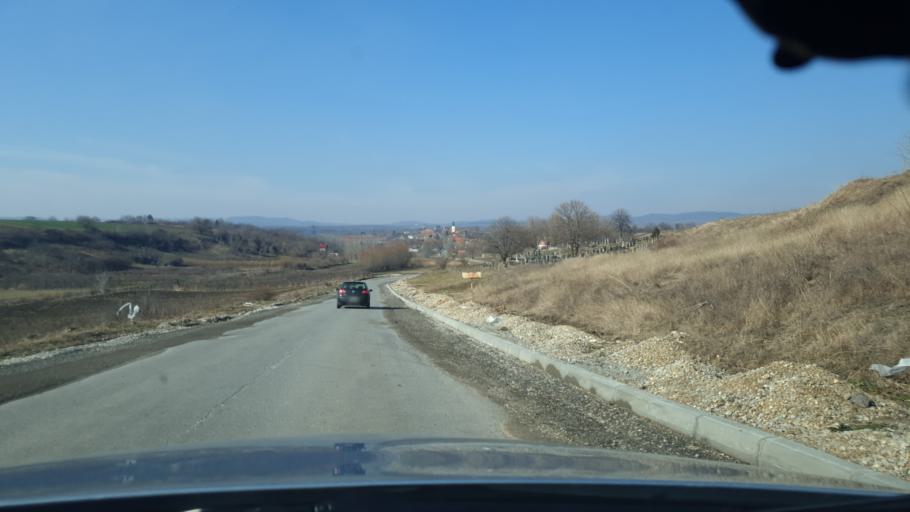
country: RS
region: Autonomna Pokrajina Vojvodina
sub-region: Sremski Okrug
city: Irig
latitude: 45.0806
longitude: 19.8417
